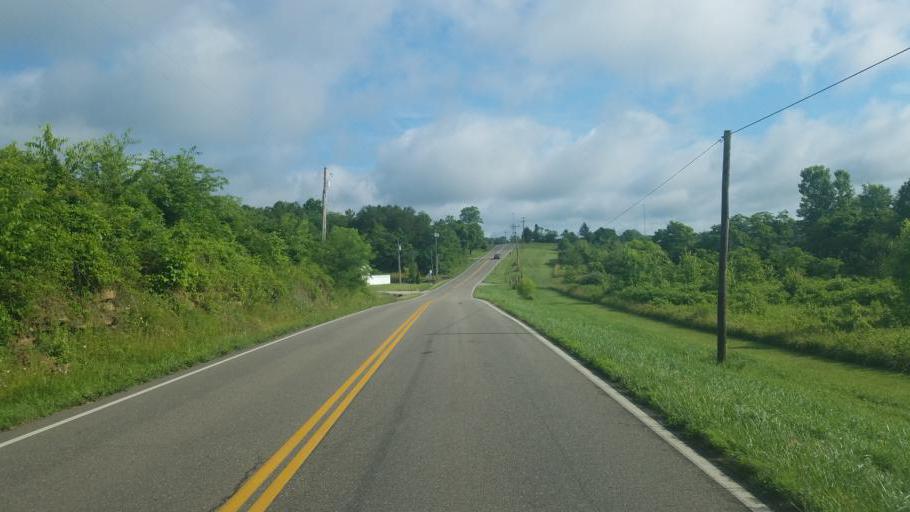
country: US
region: Ohio
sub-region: Gallia County
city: Gallipolis
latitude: 38.8736
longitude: -82.3794
